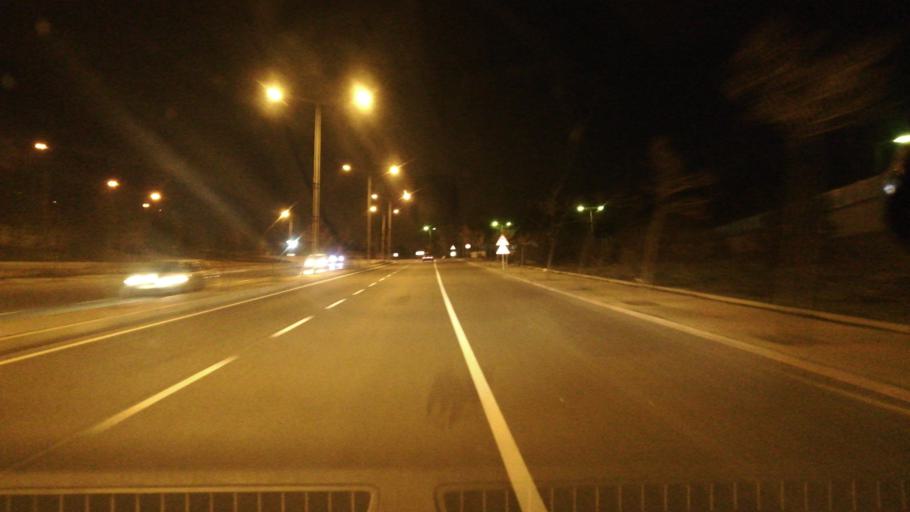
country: TR
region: Kahramanmaras
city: Kahramanmaras
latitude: 37.5976
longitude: 36.9253
